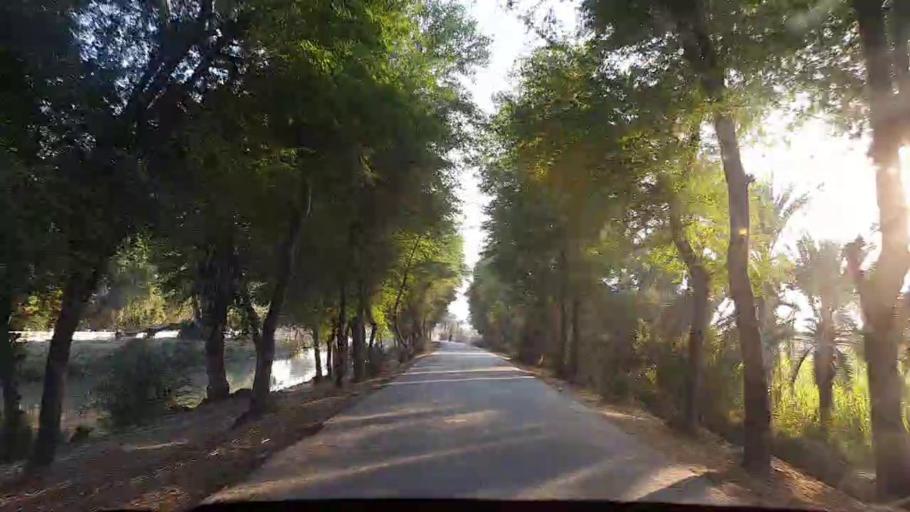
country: PK
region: Sindh
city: Sobhadero
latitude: 27.3894
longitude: 68.3835
